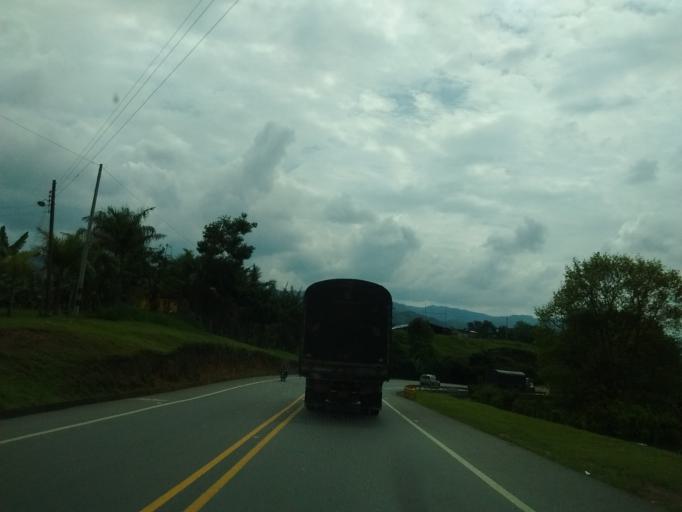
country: CO
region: Cauca
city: Morales
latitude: 2.7380
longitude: -76.5467
